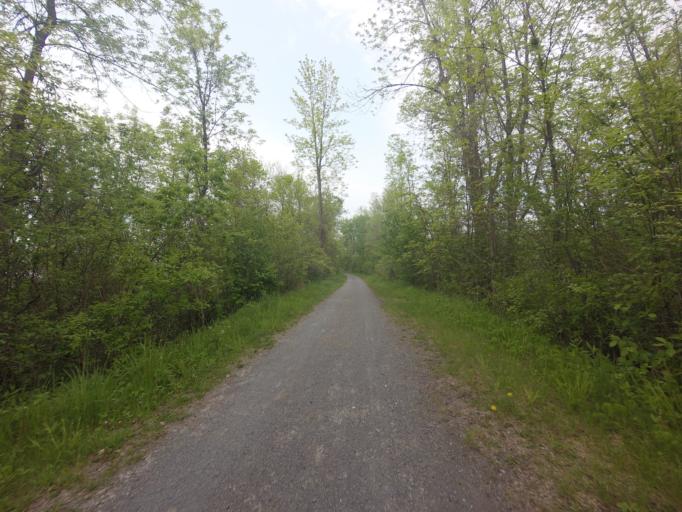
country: CA
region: Ontario
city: Kingston
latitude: 44.2885
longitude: -76.5595
